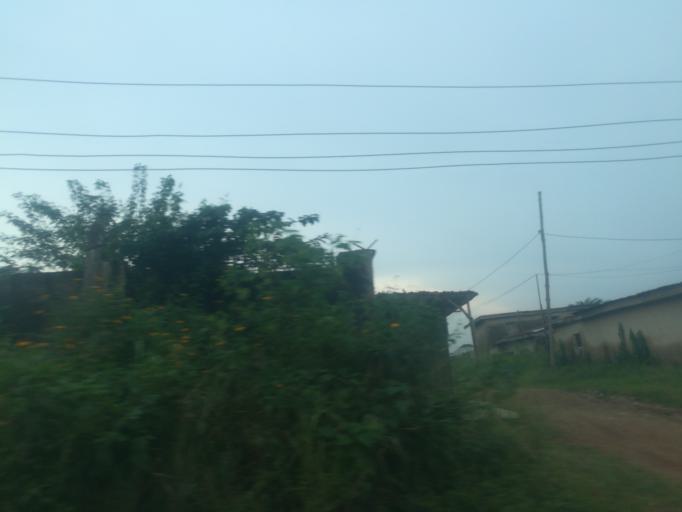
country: NG
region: Oyo
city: Ibadan
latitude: 7.3531
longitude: 3.8218
